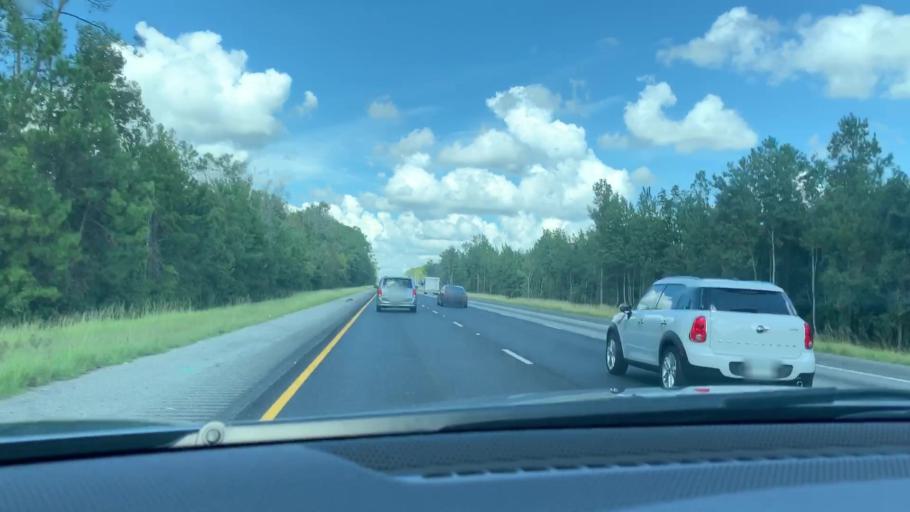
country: US
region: Georgia
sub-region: Camden County
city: Woodbine
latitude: 30.9148
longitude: -81.6859
